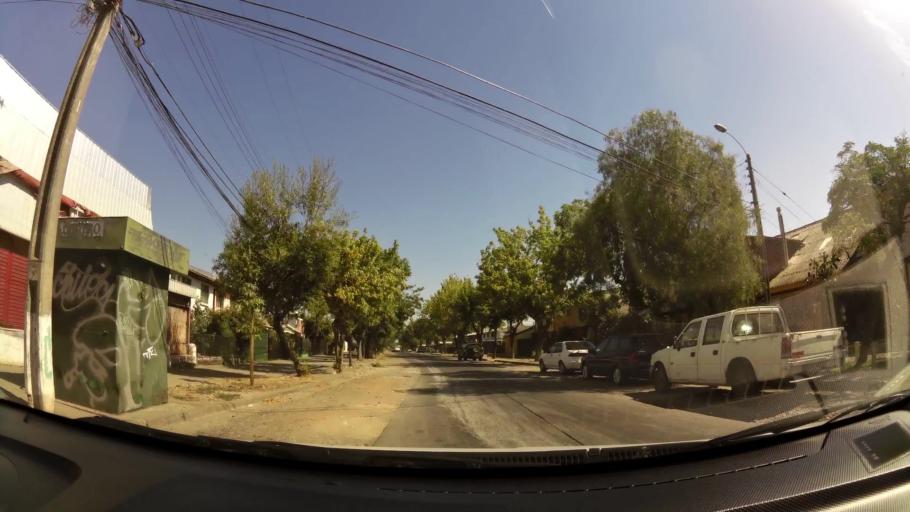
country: CL
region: Maule
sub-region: Provincia de Talca
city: Talca
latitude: -35.4337
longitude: -71.6603
